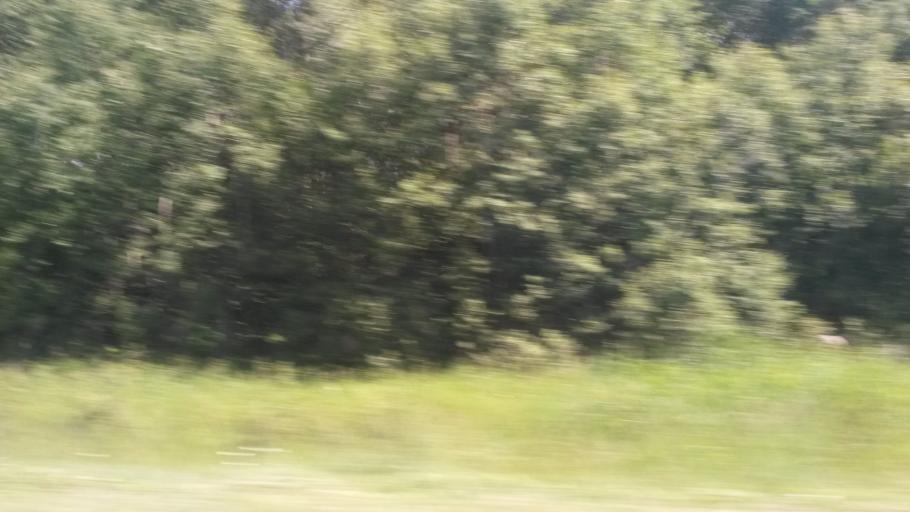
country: RU
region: Ivanovo
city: Rodniki
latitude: 57.1098
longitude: 41.7811
